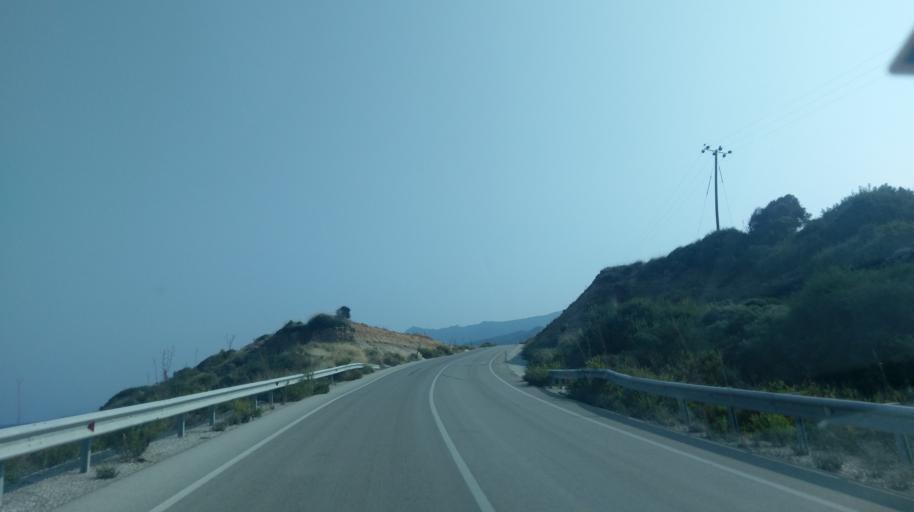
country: CY
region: Ammochostos
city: Trikomo
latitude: 35.4107
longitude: 33.8315
